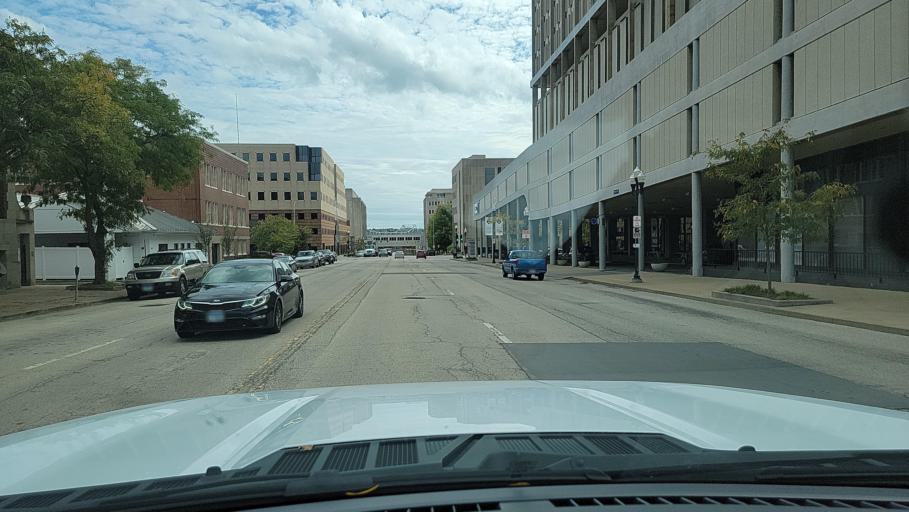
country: US
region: Illinois
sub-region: Peoria County
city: Peoria
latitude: 40.6945
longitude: -89.5903
